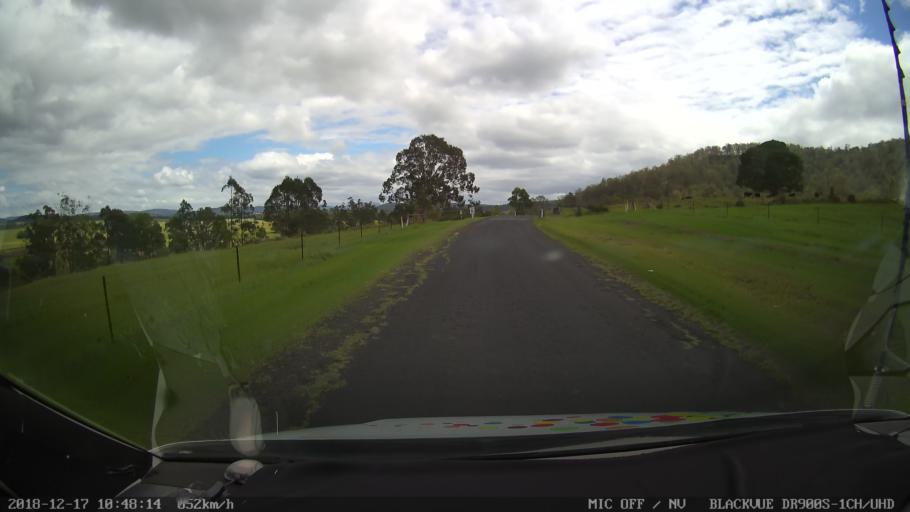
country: AU
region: New South Wales
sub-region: Clarence Valley
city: Gordon
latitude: -28.8745
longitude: 152.5707
